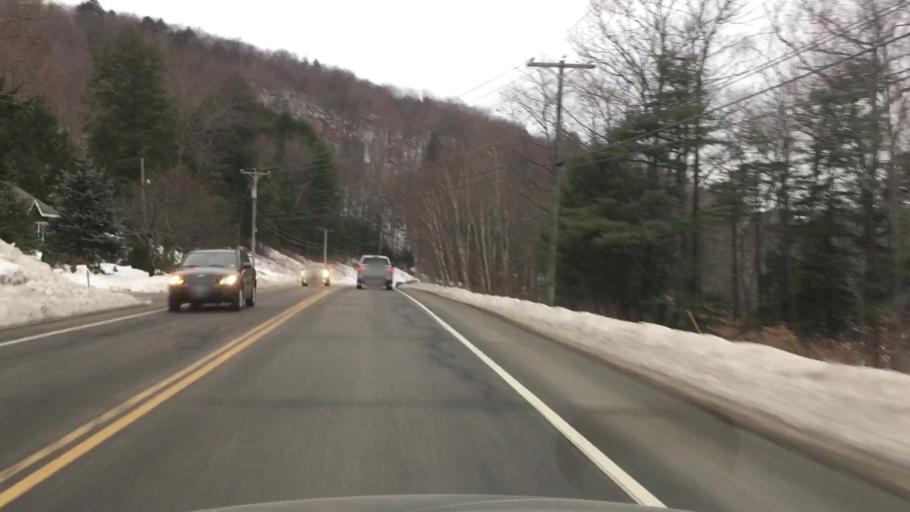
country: US
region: New Hampshire
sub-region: Merrimack County
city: Newbury
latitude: 43.3358
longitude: -72.0524
